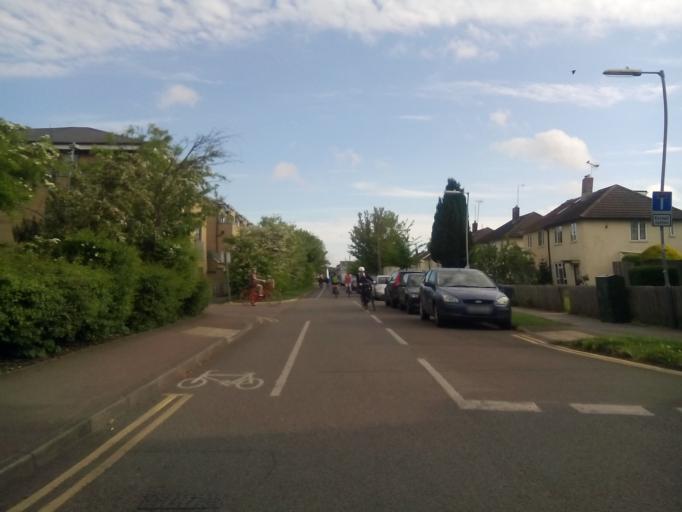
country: GB
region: England
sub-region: Cambridgeshire
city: Cambridge
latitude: 52.1937
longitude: 0.1413
